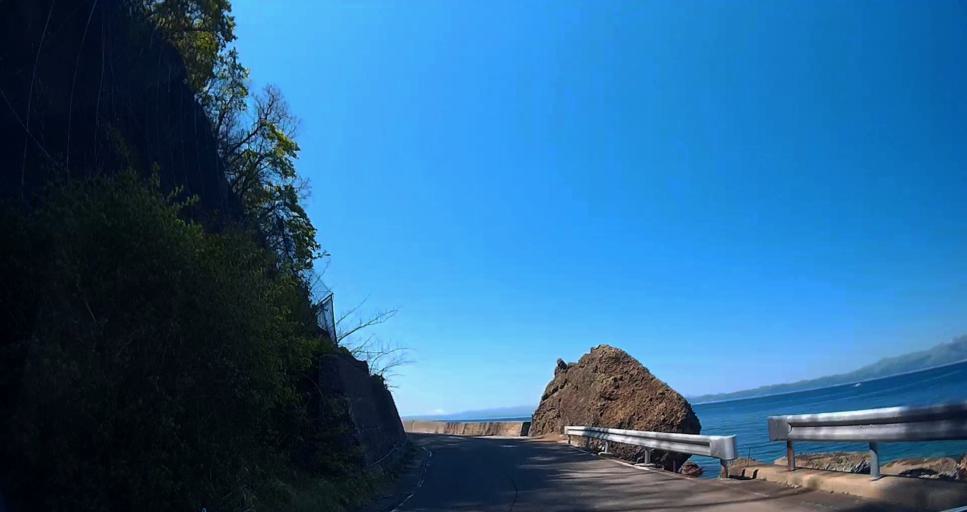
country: JP
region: Aomori
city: Aomori Shi
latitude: 41.1368
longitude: 140.7781
